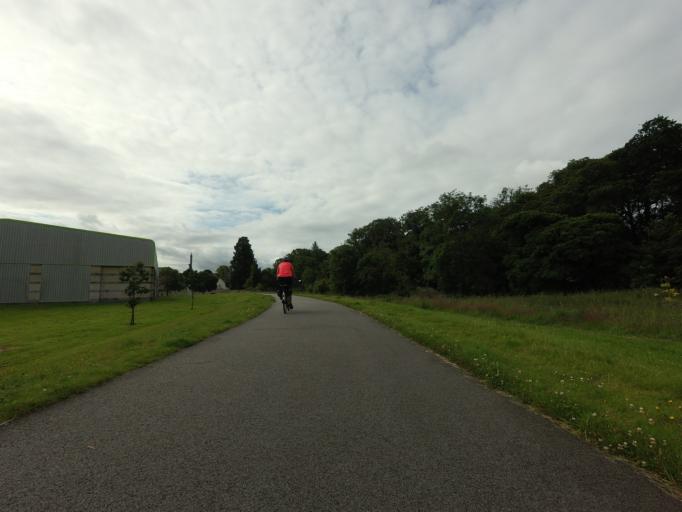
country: GB
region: Scotland
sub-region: Moray
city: Elgin
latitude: 57.6521
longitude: -3.3252
